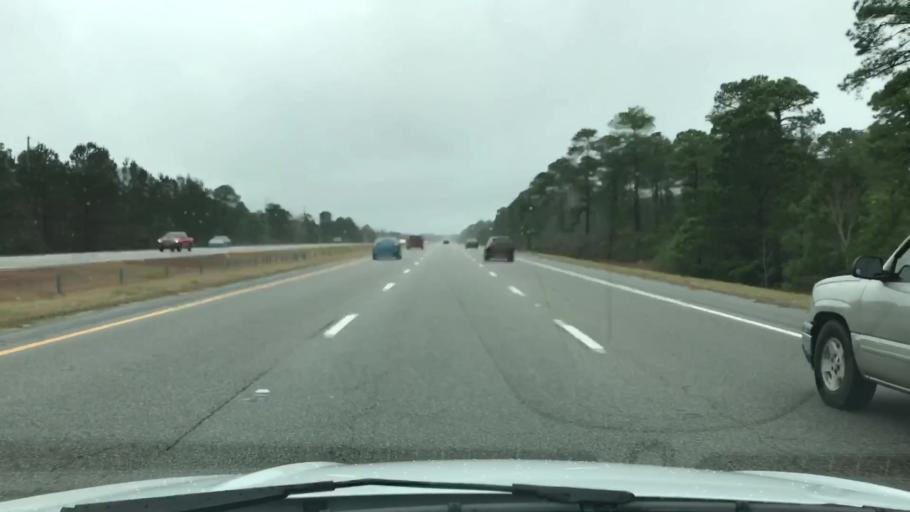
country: US
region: South Carolina
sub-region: Horry County
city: Forestbrook
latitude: 33.7482
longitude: -78.9083
